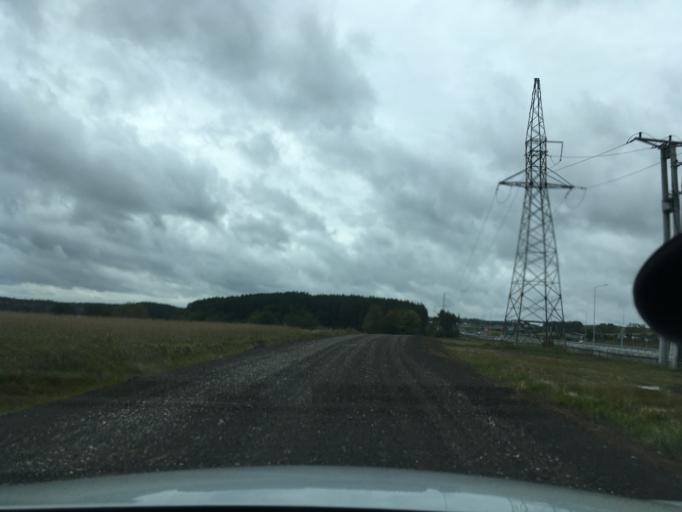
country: PL
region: Pomeranian Voivodeship
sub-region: Powiat koscierski
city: Koscierzyna
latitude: 54.1108
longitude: 17.9975
